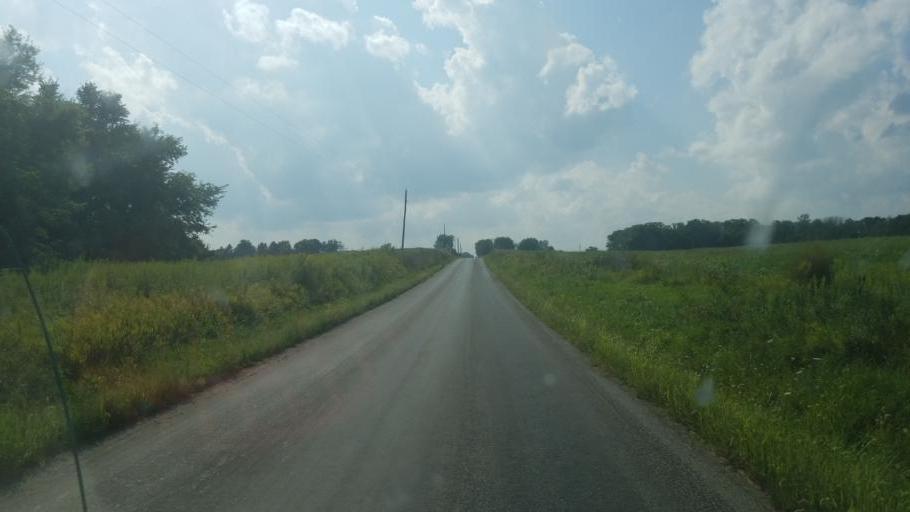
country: US
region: Ohio
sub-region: Wayne County
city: West Salem
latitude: 40.9524
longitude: -82.0480
